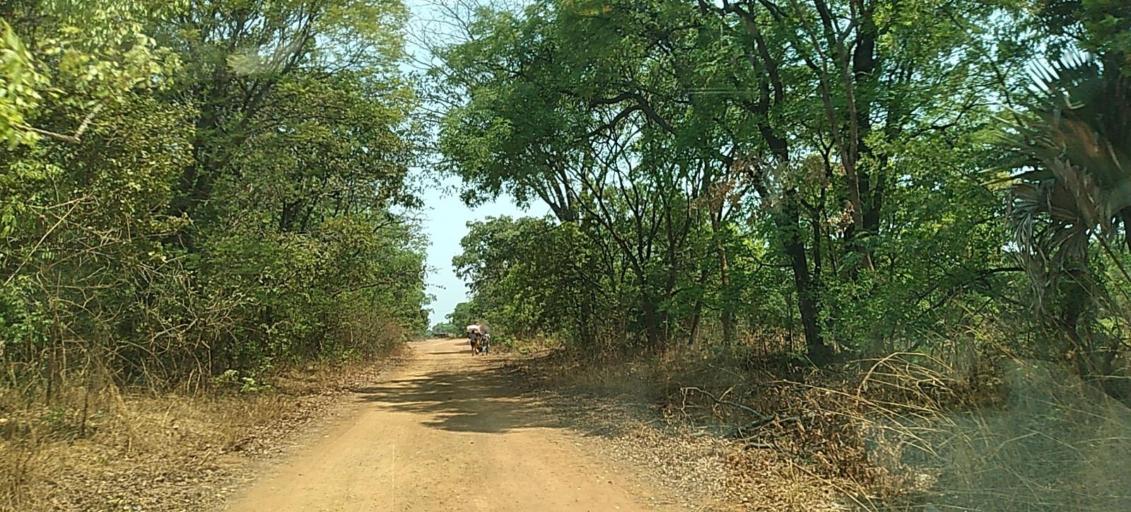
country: ZM
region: Copperbelt
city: Ndola
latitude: -13.0548
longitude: 28.7373
